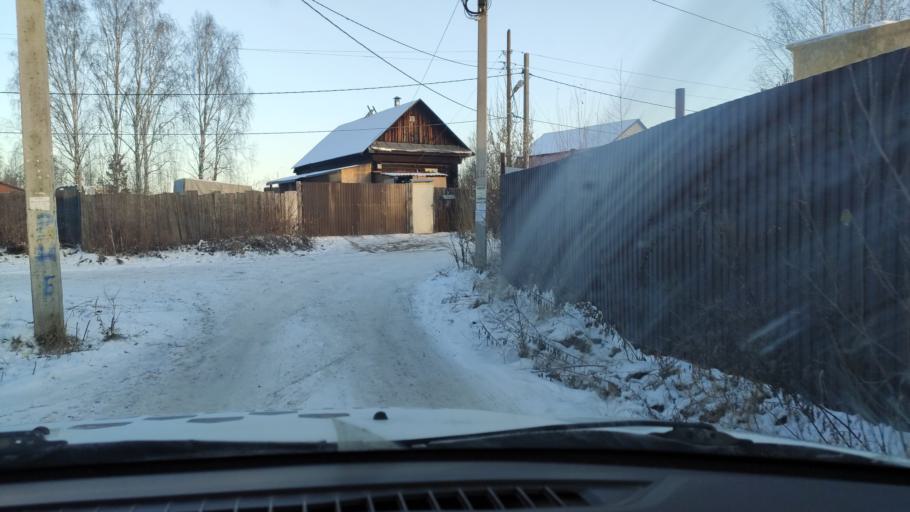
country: RU
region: Perm
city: Perm
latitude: 58.0321
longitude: 56.2289
